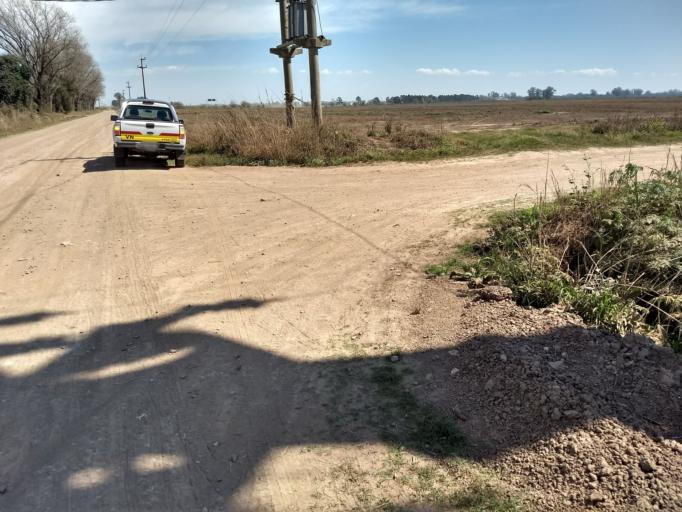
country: AR
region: Santa Fe
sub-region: Departamento de San Lorenzo
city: San Lorenzo
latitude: -32.6658
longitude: -60.8092
